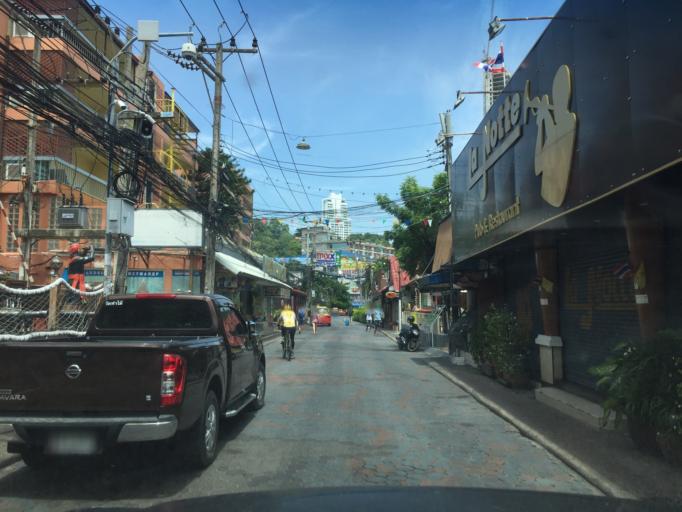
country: TH
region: Chon Buri
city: Phatthaya
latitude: 12.9250
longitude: 100.8701
